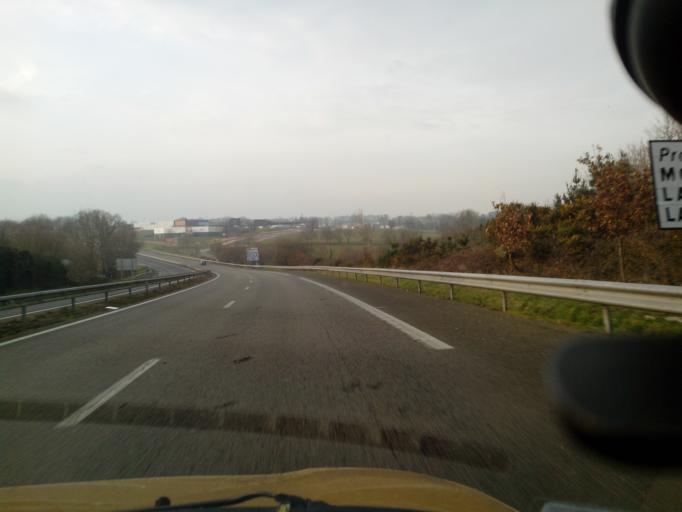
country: FR
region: Brittany
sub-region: Departement du Morbihan
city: Josselin
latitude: 47.9609
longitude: -2.5379
